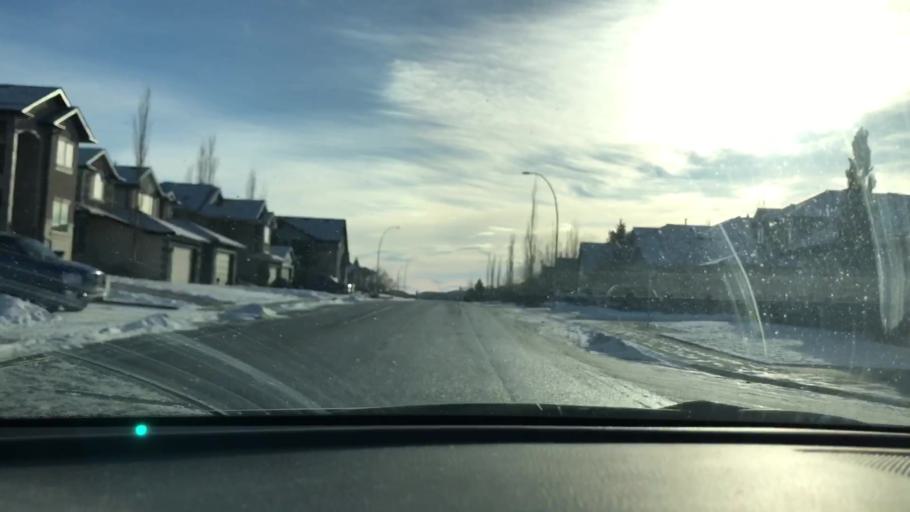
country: CA
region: Alberta
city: Calgary
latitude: 51.0252
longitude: -114.1773
